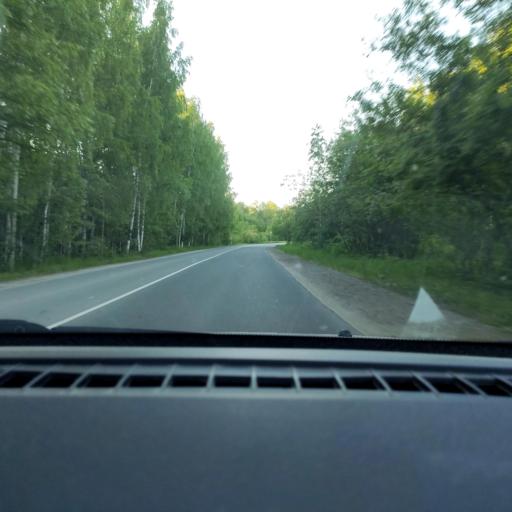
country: RU
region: Perm
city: Polazna
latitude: 58.1221
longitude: 56.4327
